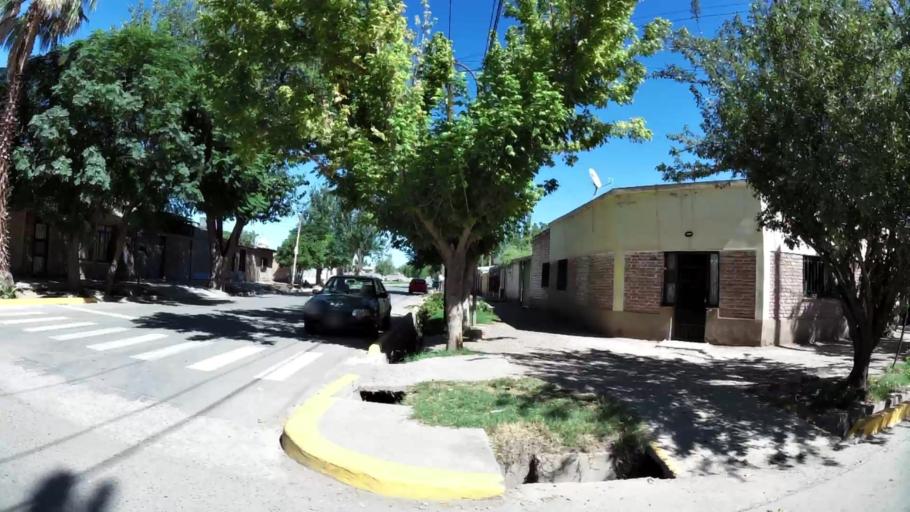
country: AR
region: Mendoza
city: Las Heras
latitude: -32.8342
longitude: -68.8418
